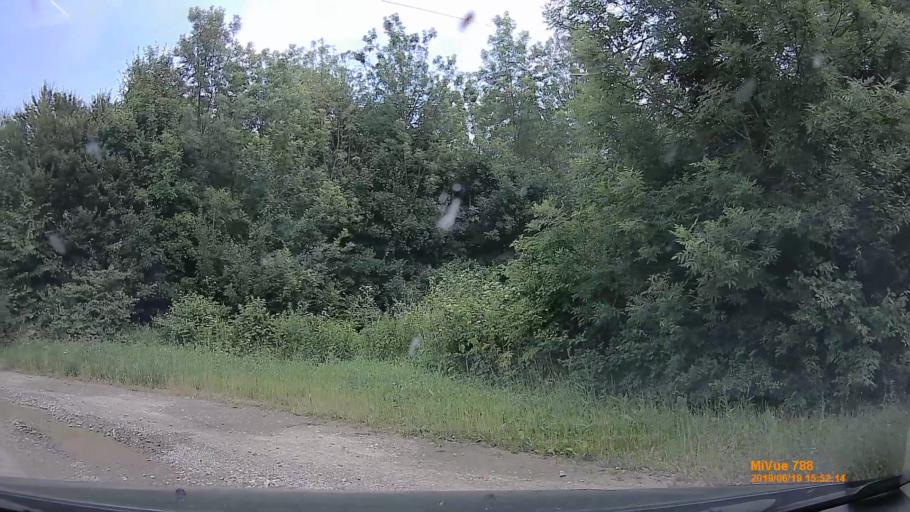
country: HU
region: Baranya
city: Szigetvar
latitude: 46.0263
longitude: 17.7465
